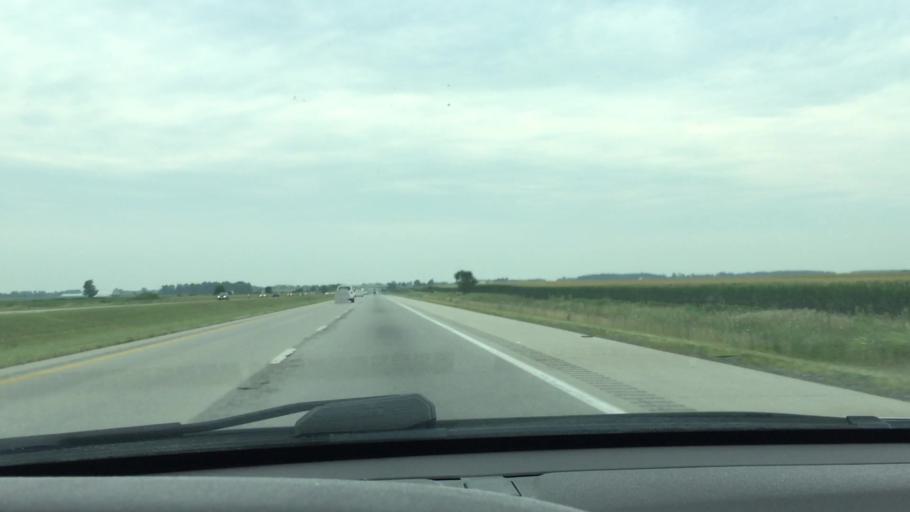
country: US
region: Ohio
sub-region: Greene County
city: Shawnee Hills
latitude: 39.5424
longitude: -83.7634
